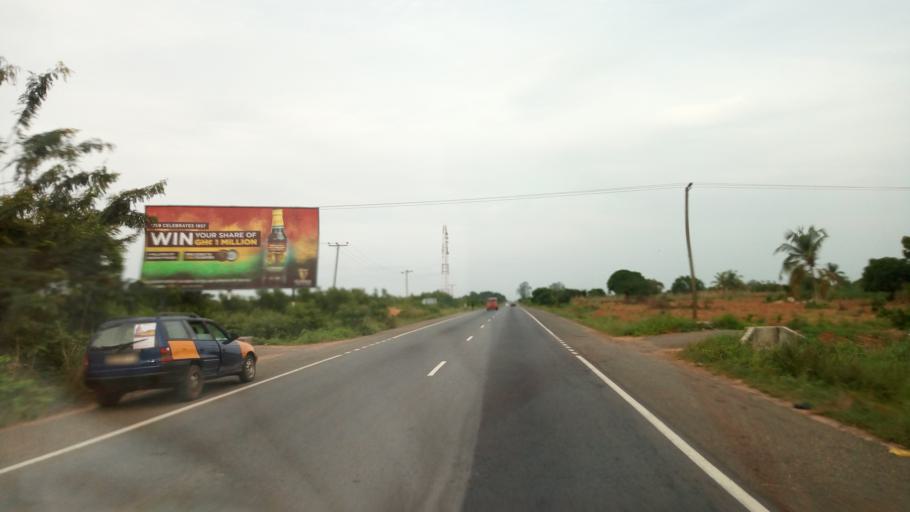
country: GH
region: Volta
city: Keta
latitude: 6.0642
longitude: 1.0074
